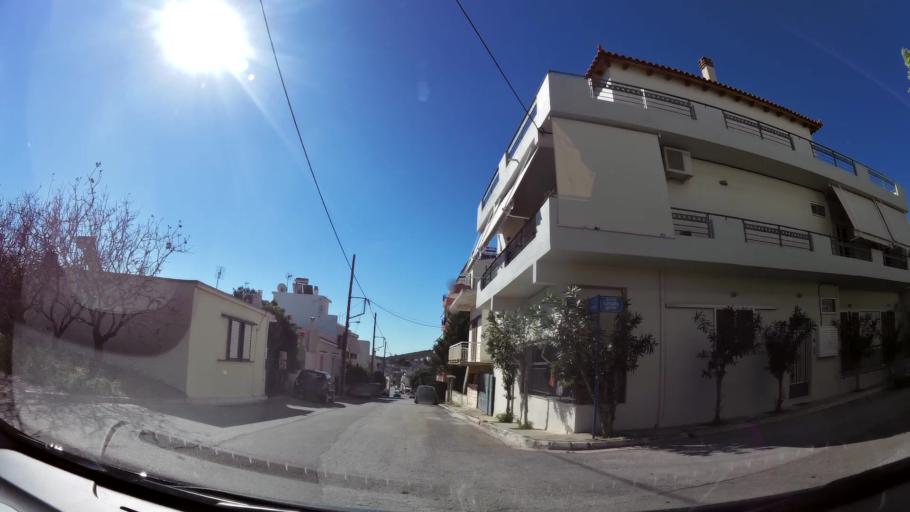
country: GR
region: Attica
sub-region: Nomarchia Anatolikis Attikis
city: Koropi
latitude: 37.9003
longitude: 23.8822
